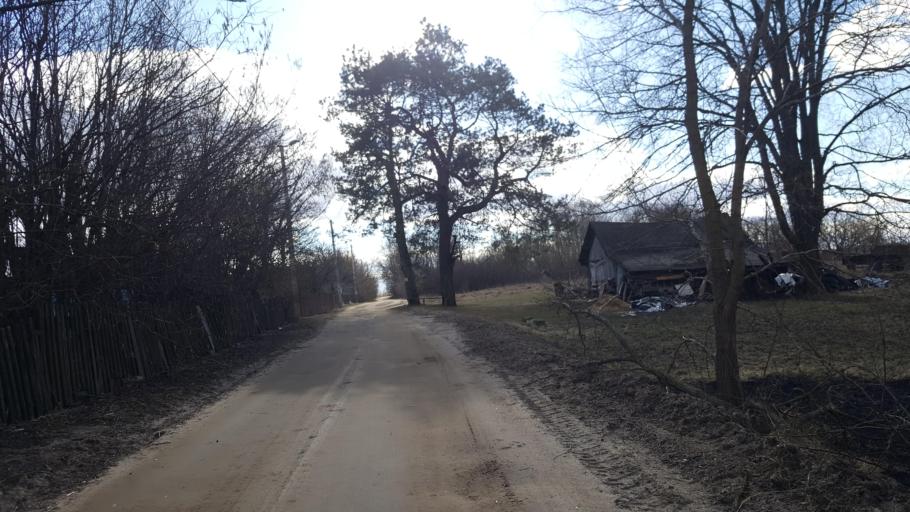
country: BY
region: Brest
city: Kamyanyets
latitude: 52.3921
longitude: 23.8846
